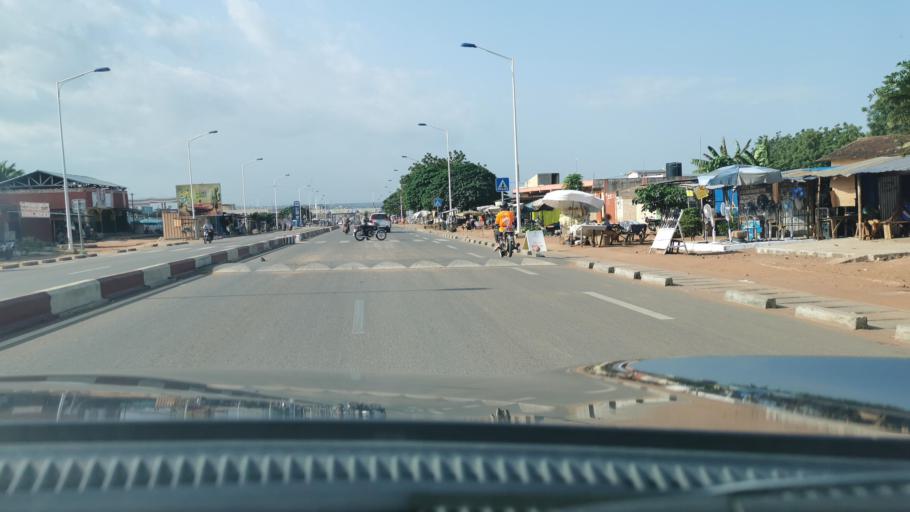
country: TG
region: Maritime
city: Lome
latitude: 6.2080
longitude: 1.2433
